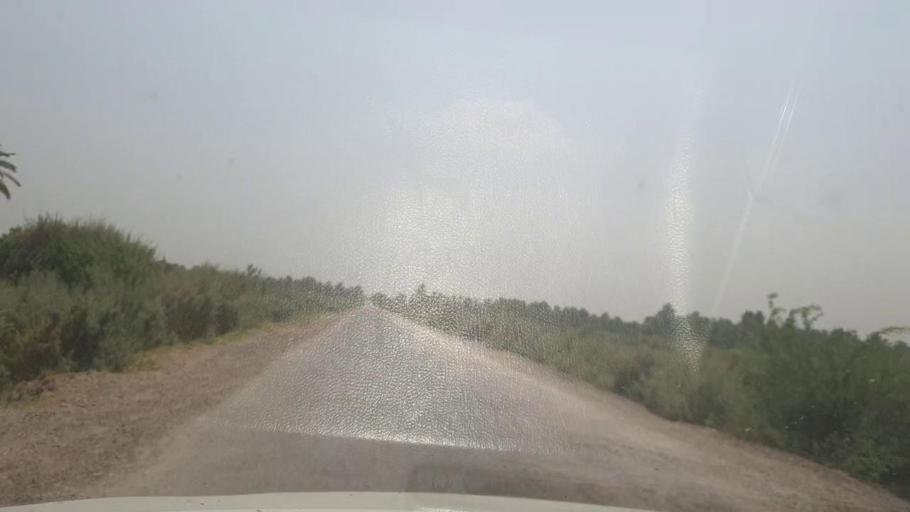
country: PK
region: Sindh
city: Kot Diji
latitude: 27.3752
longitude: 68.7061
